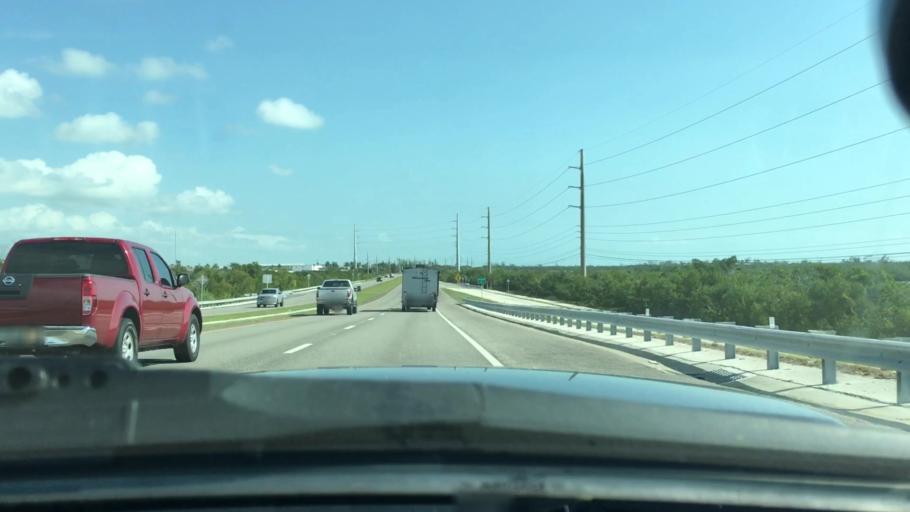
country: US
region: Florida
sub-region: Monroe County
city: Big Coppitt Key
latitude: 24.5886
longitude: -81.6895
